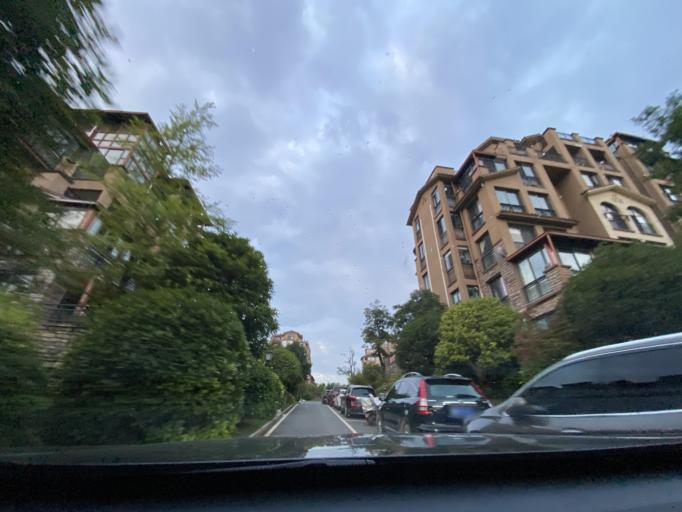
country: CN
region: Guizhou Sheng
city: Changqi
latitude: 28.5409
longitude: 105.9864
